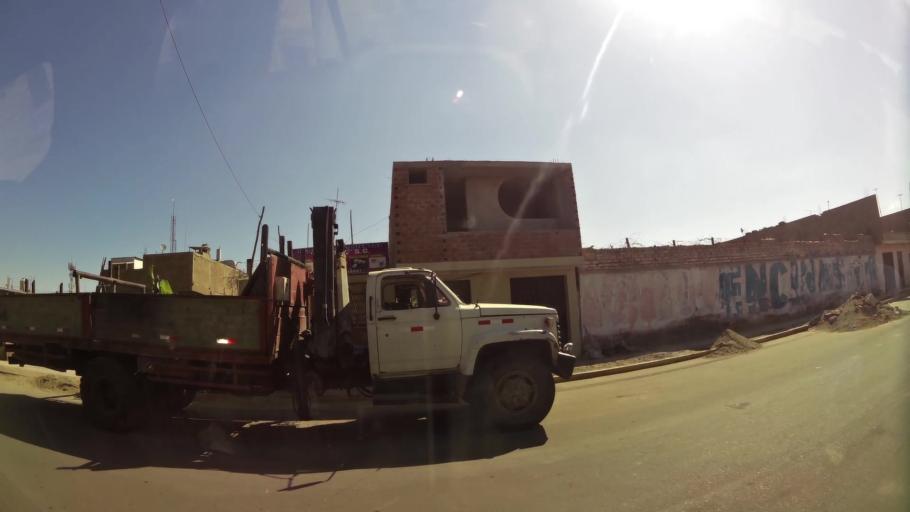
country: PE
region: Ica
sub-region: Provincia de Ica
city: La Tinguina
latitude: -14.0357
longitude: -75.7064
